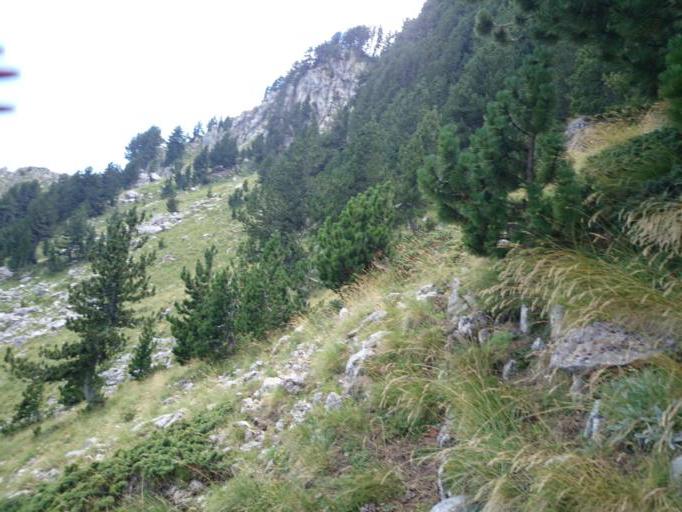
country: AL
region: Berat
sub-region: Rrethi i Beratit
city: Polican
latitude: 40.6592
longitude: 20.1579
